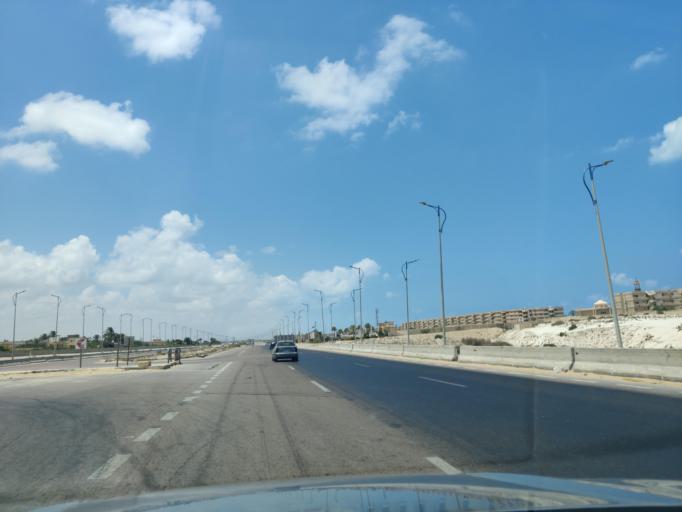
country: EG
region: Muhafazat Matruh
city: Al `Alamayn
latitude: 30.9251
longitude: 29.4652
